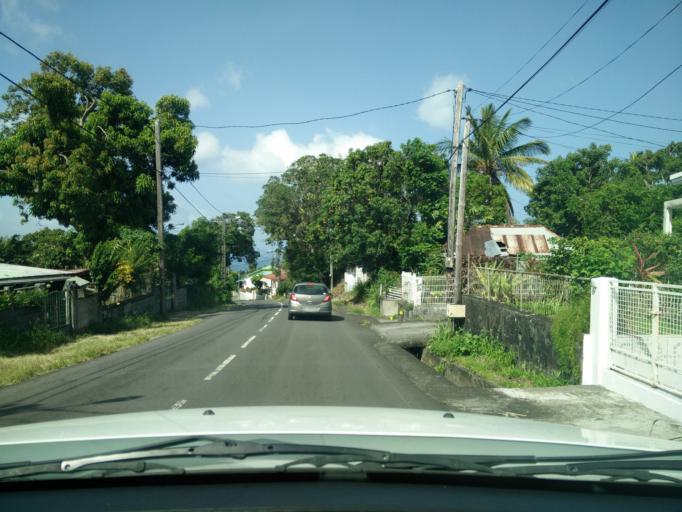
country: GP
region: Guadeloupe
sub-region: Guadeloupe
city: Gourbeyre
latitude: 15.9944
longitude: -61.7056
